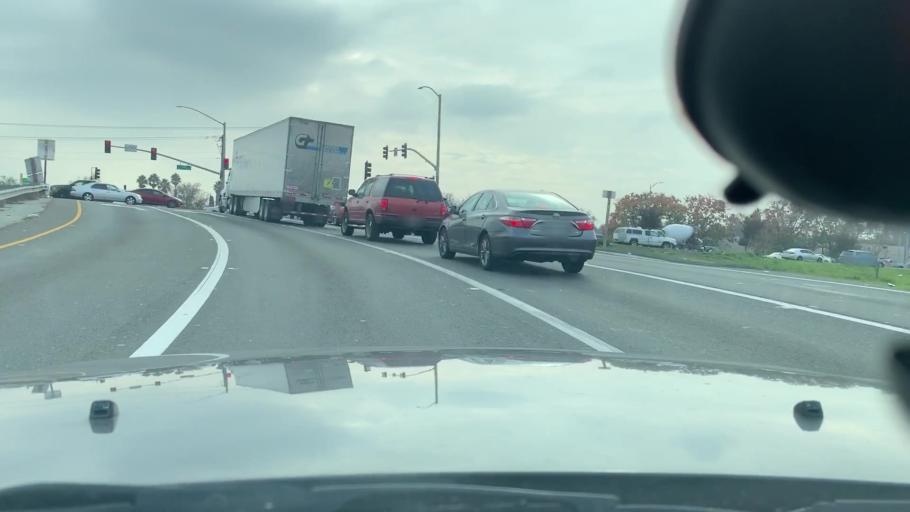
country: US
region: California
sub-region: Santa Clara County
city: Seven Trees
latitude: 37.3182
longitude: -121.8332
